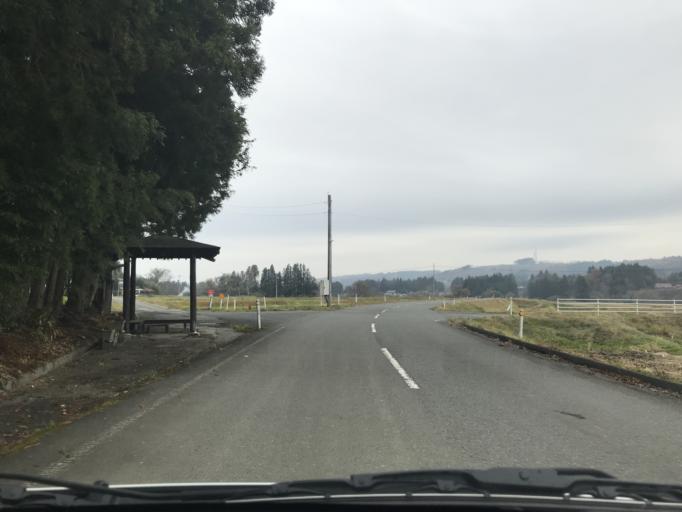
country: JP
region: Iwate
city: Ichinoseki
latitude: 39.0240
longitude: 141.0734
